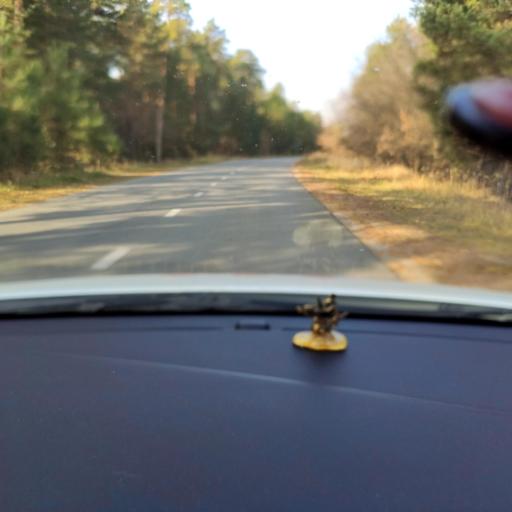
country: RU
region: Tatarstan
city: Staroye Arakchino
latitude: 55.8240
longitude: 48.9140
